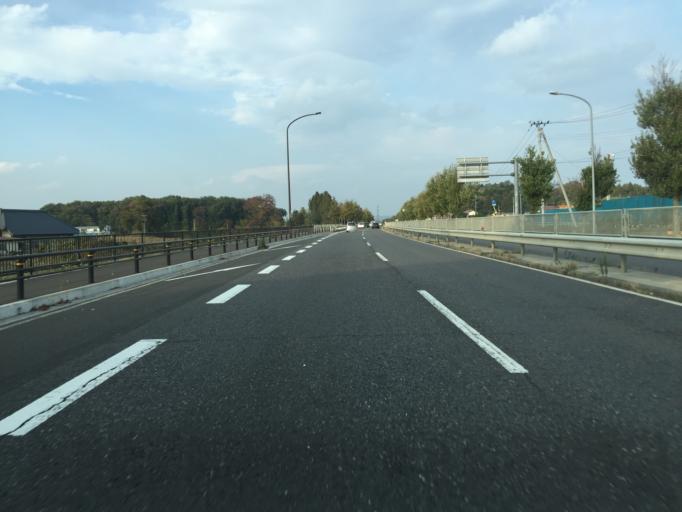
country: JP
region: Fukushima
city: Nihommatsu
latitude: 37.6378
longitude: 140.4833
